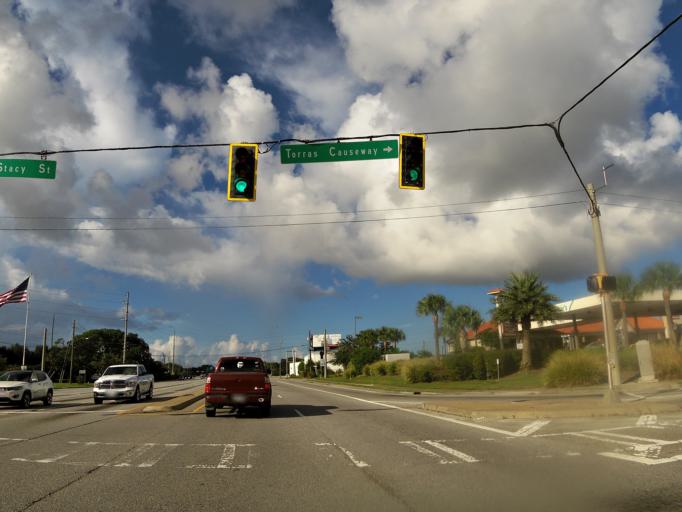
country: US
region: Georgia
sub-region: Glynn County
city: Brunswick
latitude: 31.1619
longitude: -81.4765
